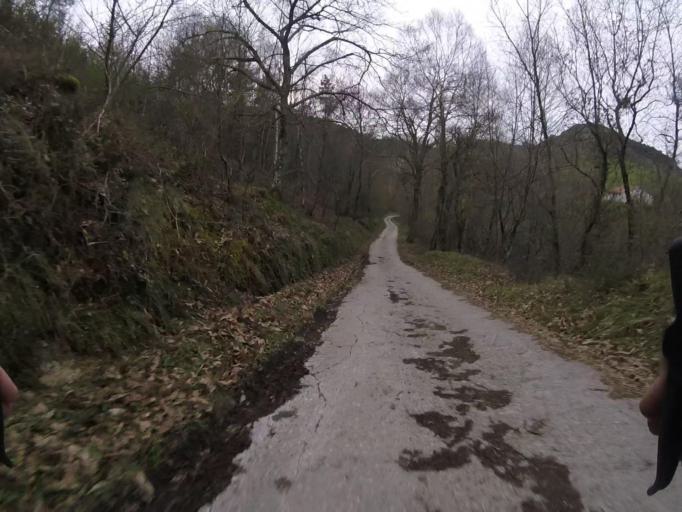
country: ES
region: Navarre
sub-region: Provincia de Navarra
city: Lesaka
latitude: 43.2722
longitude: -1.7528
